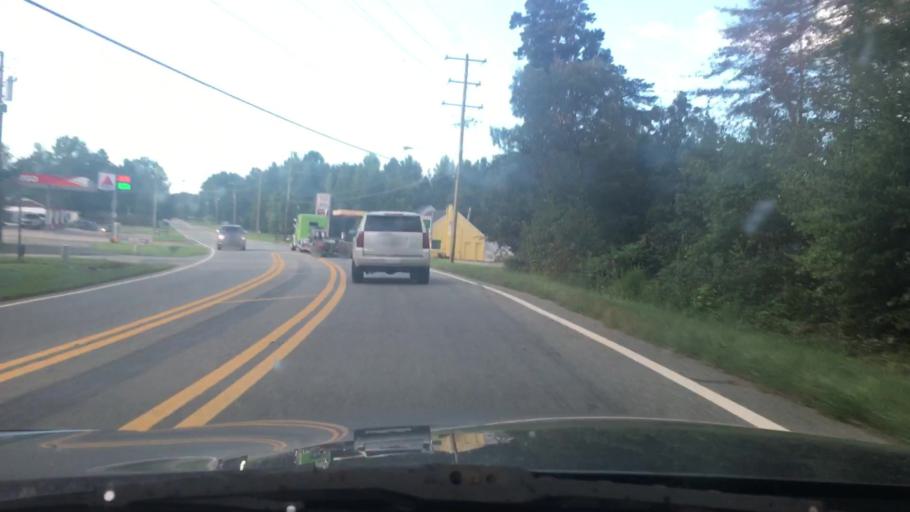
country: US
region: North Carolina
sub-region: Alamance County
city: Green Level
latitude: 36.1393
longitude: -79.3448
